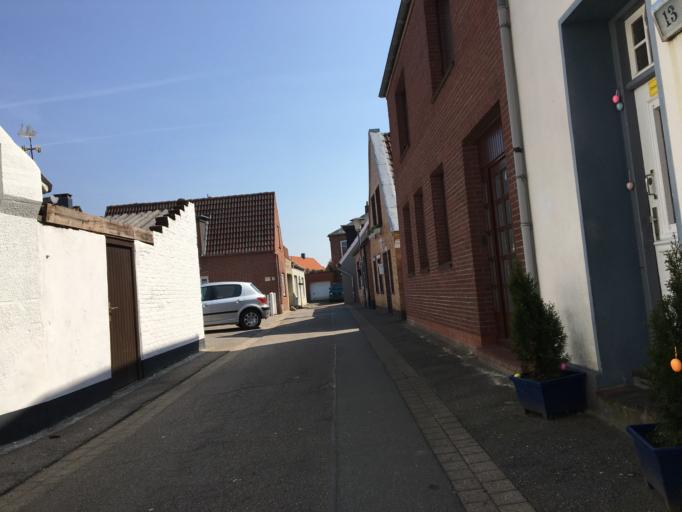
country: DE
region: Schleswig-Holstein
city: Tonning
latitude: 54.3182
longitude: 8.9406
